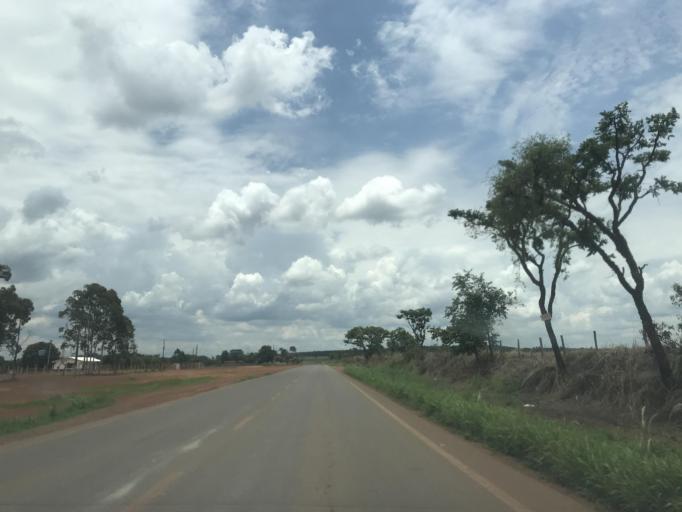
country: BR
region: Goias
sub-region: Vianopolis
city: Vianopolis
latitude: -16.7400
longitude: -48.4760
